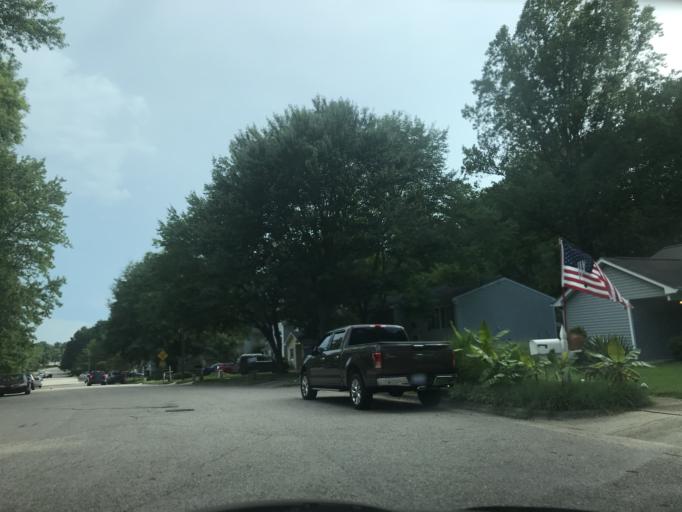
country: US
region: North Carolina
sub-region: Wake County
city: Raleigh
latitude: 35.8316
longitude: -78.5864
